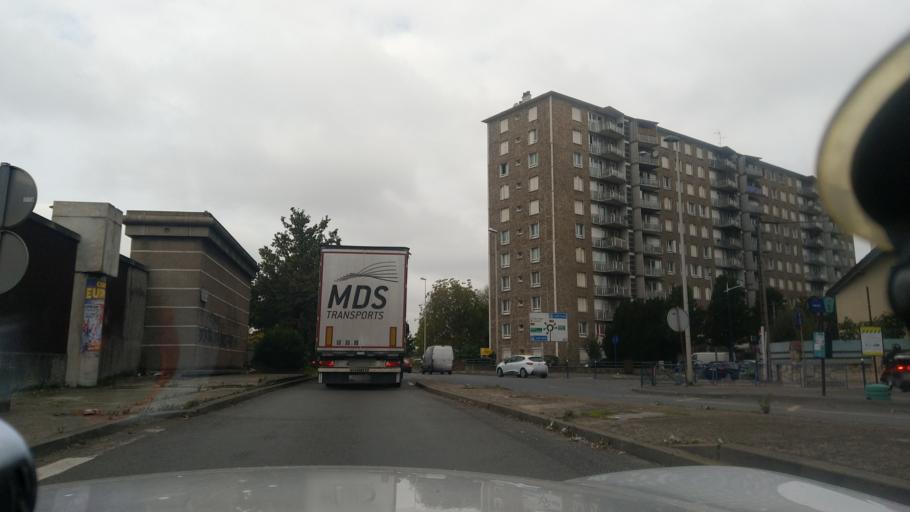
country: FR
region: Ile-de-France
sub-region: Departement de Seine-Saint-Denis
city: Drancy
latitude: 48.9142
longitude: 2.4333
